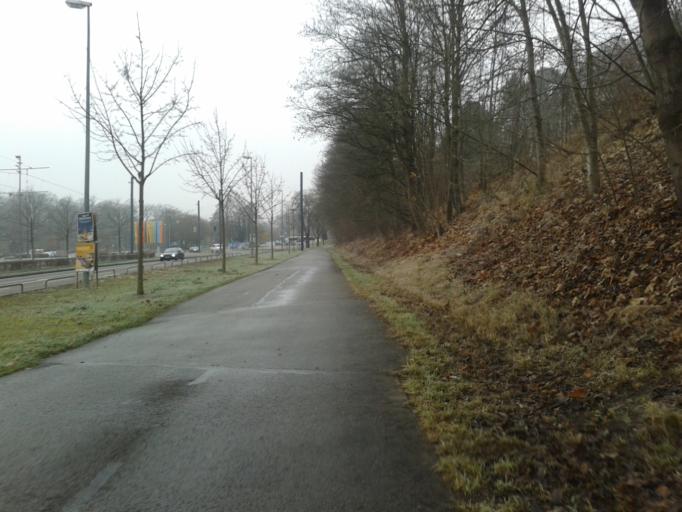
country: DE
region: Bavaria
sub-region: Swabia
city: Neu-Ulm
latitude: 48.4136
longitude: 10.0110
